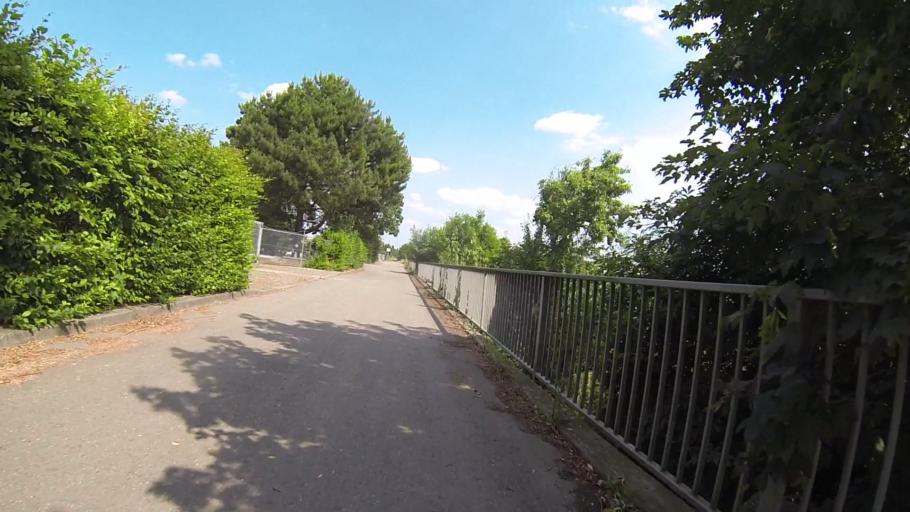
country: DE
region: Baden-Wuerttemberg
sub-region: Regierungsbezirk Stuttgart
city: Niederstotzingen
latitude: 48.5330
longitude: 10.2415
